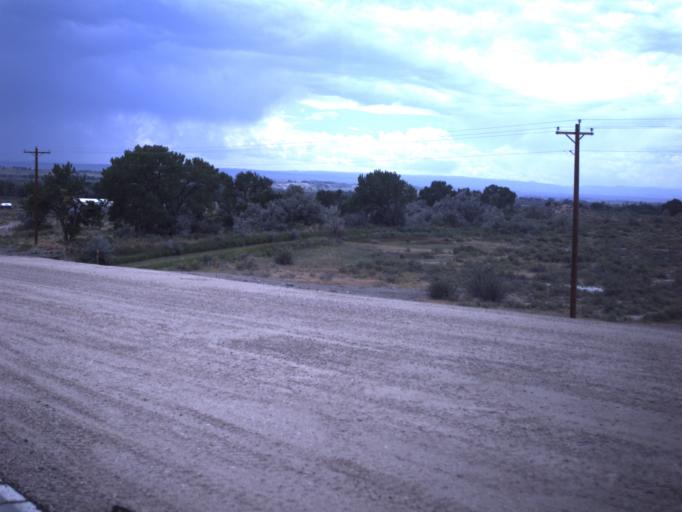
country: US
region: Utah
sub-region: Duchesne County
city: Roosevelt
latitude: 40.2155
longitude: -110.0674
